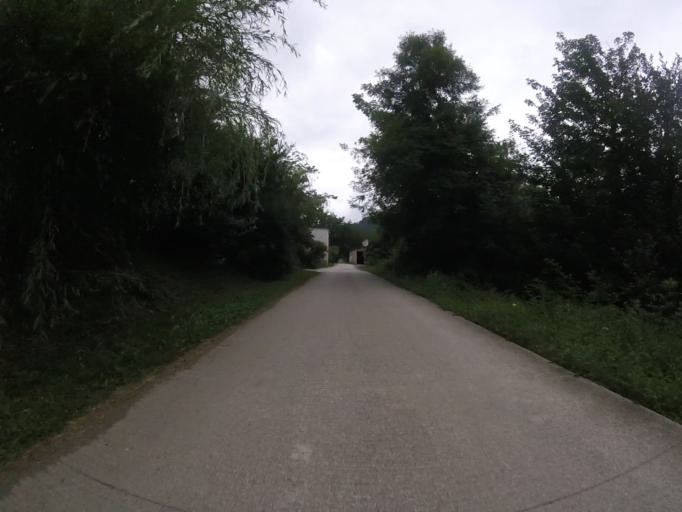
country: ES
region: Navarre
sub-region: Provincia de Navarra
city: Sunbilla
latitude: 43.1602
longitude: -1.6718
